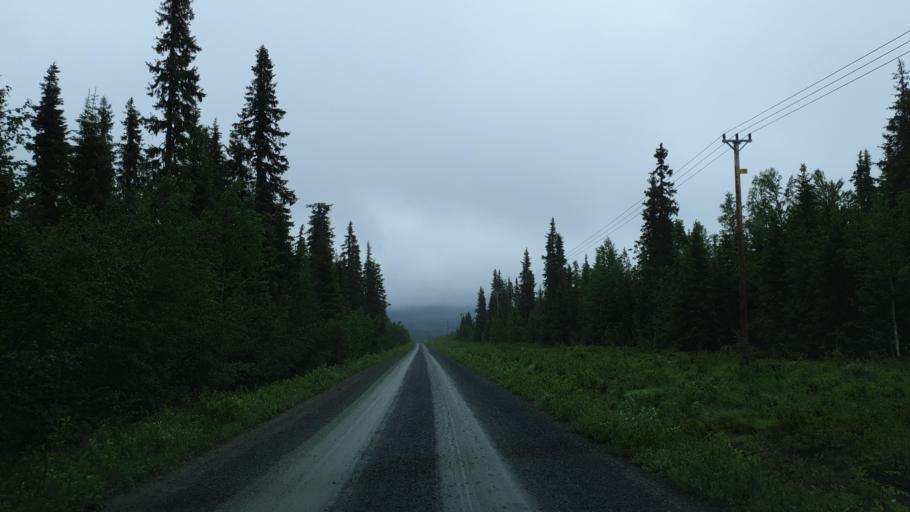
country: SE
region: Vaesterbotten
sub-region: Vilhelmina Kommun
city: Sjoberg
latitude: 65.3106
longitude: 15.9765
